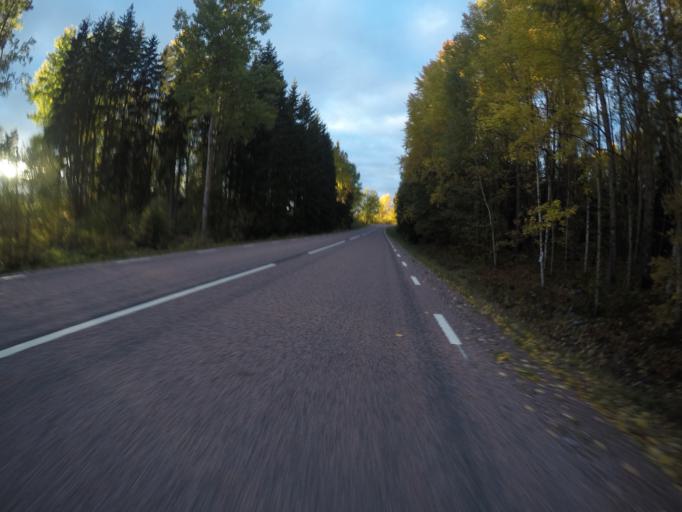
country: SE
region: Vaestmanland
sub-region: Arboga Kommun
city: Tyringe
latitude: 59.3107
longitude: 15.9889
